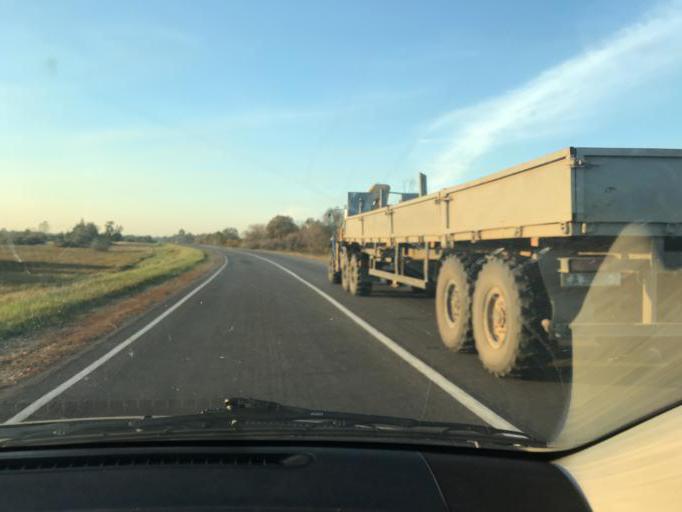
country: BY
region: Brest
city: Pinsk
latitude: 52.0800
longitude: 26.1431
